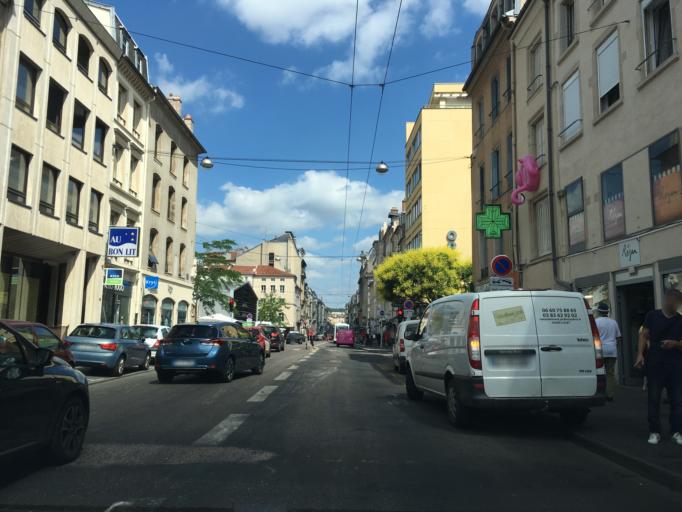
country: FR
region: Lorraine
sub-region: Departement de Meurthe-et-Moselle
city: Nancy
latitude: 48.6889
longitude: 6.1839
